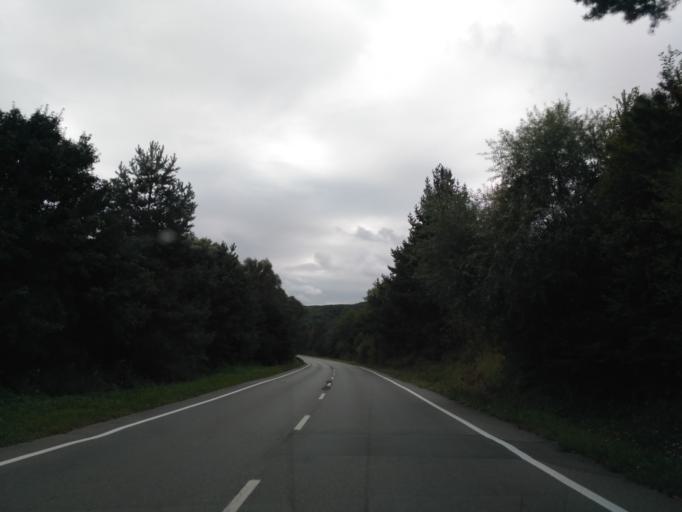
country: SK
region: Presovsky
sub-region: Okres Presov
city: Presov
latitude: 48.9600
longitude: 21.1636
